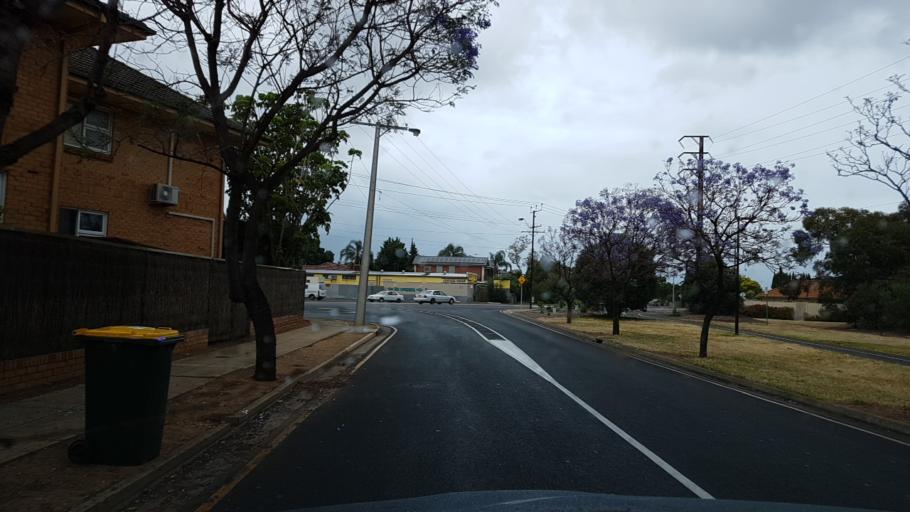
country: AU
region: South Australia
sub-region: Marion
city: South Plympton
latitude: -34.9677
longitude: 138.5477
